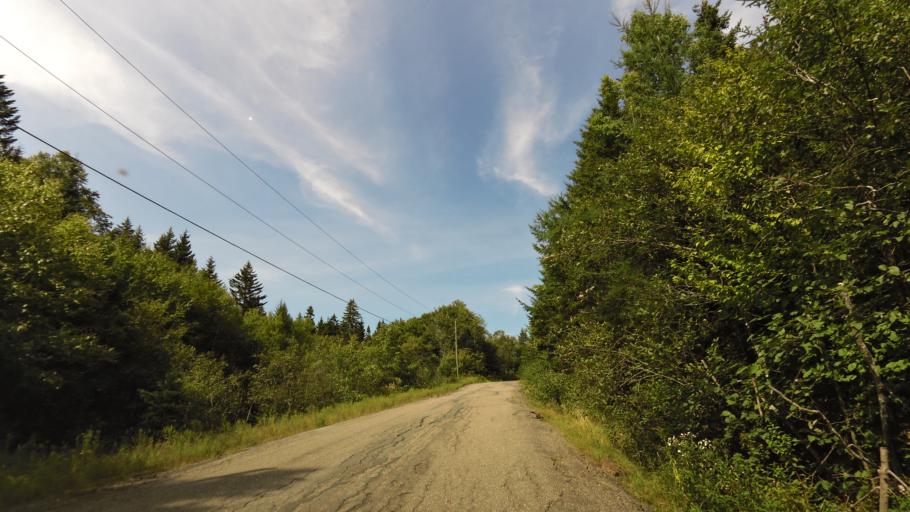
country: CA
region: New Brunswick
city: Hampton
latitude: 45.5565
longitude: -65.8427
